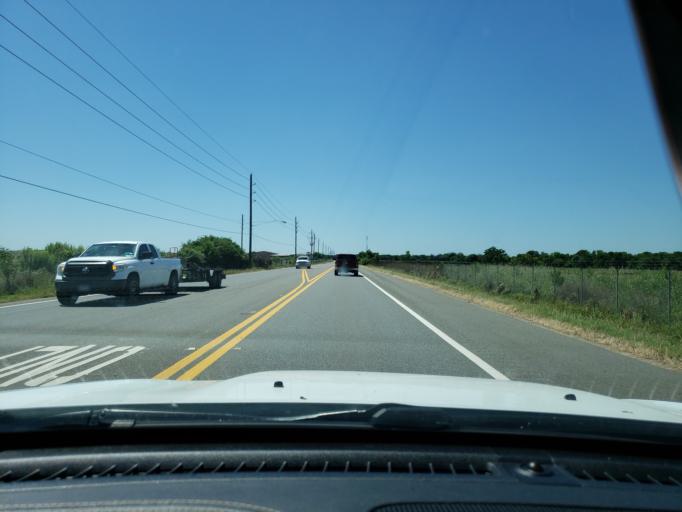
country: US
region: Texas
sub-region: Fort Bend County
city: Fulshear
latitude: 29.6791
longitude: -95.8390
